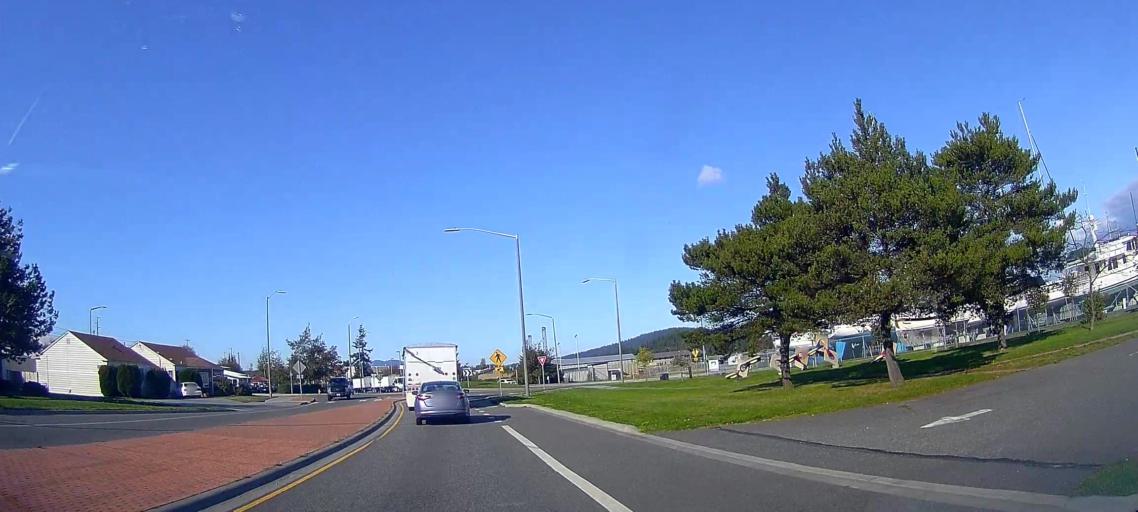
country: US
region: Washington
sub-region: Skagit County
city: Anacortes
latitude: 48.5038
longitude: -122.6094
